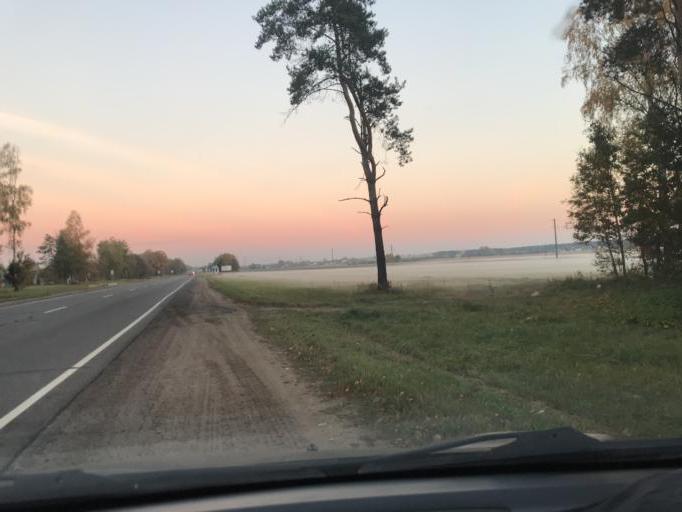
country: BY
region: Mogilev
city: Babruysk
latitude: 53.2083
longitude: 29.0841
